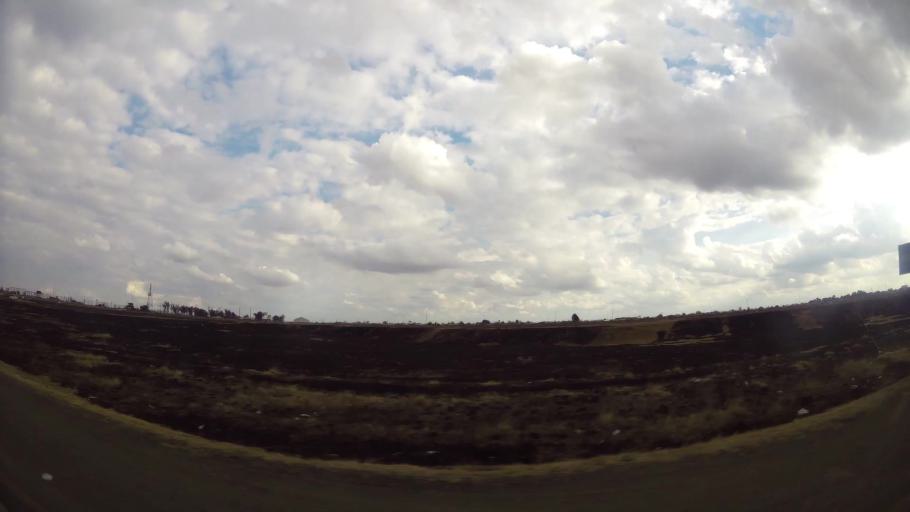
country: ZA
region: Orange Free State
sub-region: Fezile Dabi District Municipality
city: Sasolburg
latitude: -26.8397
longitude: 27.8713
